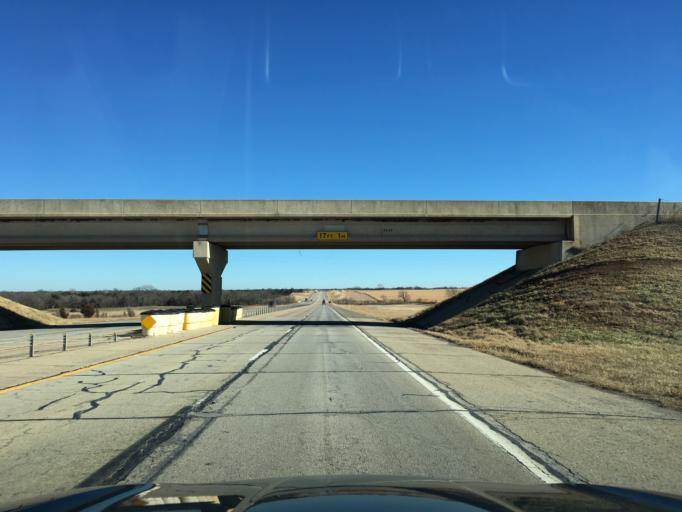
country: US
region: Oklahoma
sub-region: Pawnee County
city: Pawnee
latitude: 36.2251
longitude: -96.8553
